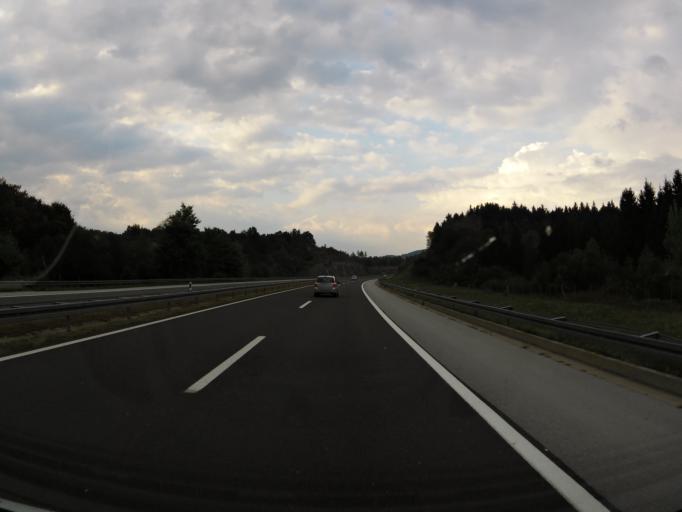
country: HR
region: Karlovacka
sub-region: Grad Ogulin
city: Ogulin
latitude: 45.3870
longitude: 15.2597
